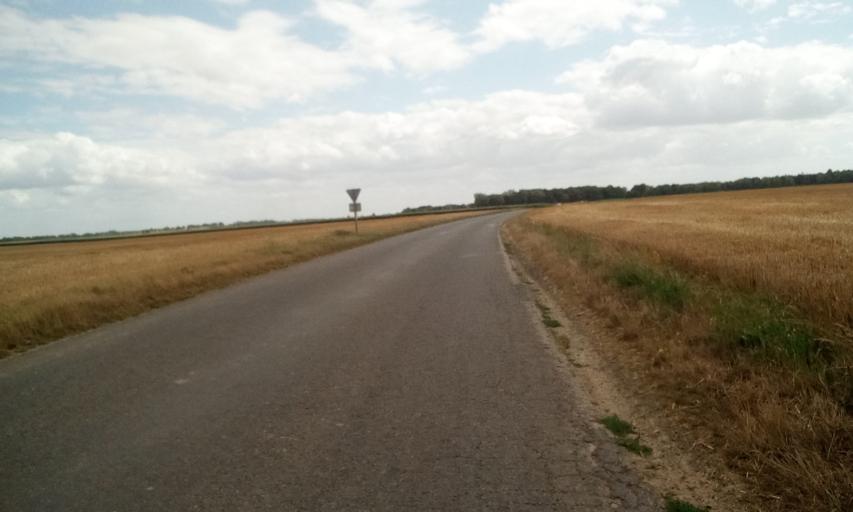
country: FR
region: Lower Normandy
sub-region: Departement du Calvados
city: Creully
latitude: 49.2794
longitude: -0.5337
